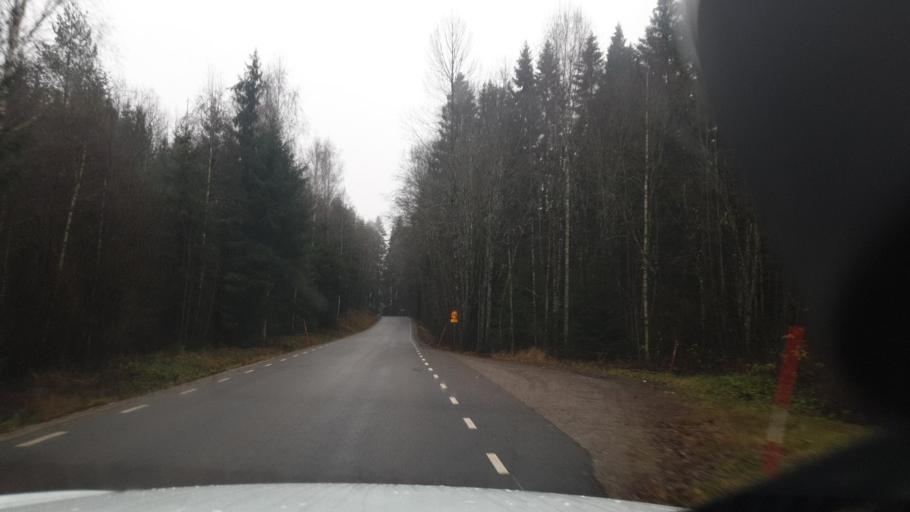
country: SE
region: Vaermland
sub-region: Arvika Kommun
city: Arvika
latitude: 59.6384
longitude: 12.8163
